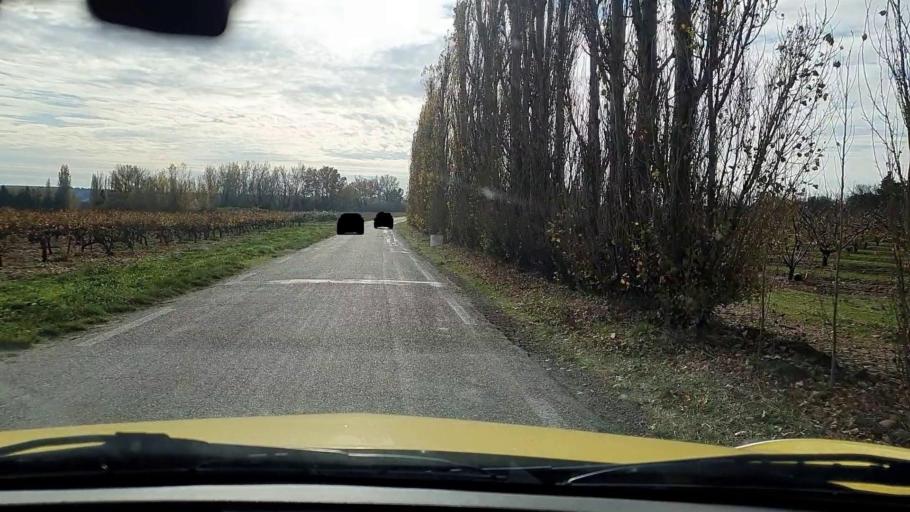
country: FR
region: Languedoc-Roussillon
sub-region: Departement du Gard
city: Jonquieres-Saint-Vincent
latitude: 43.8406
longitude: 4.5693
